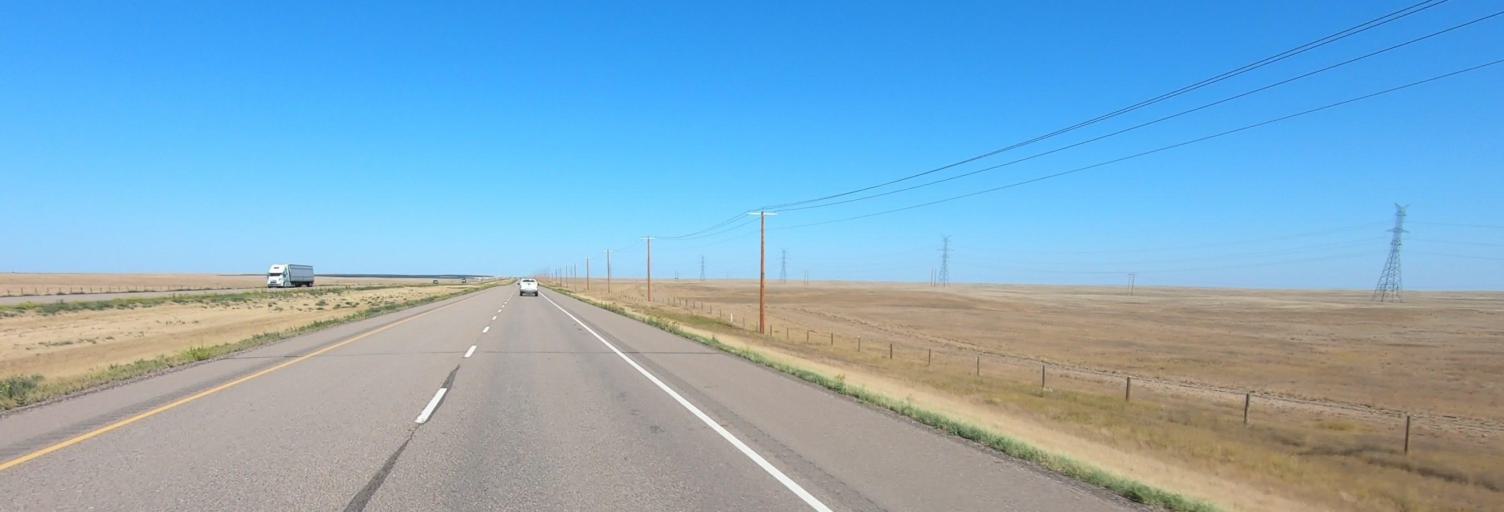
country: CA
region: Alberta
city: Bow Island
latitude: 50.2535
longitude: -111.2349
